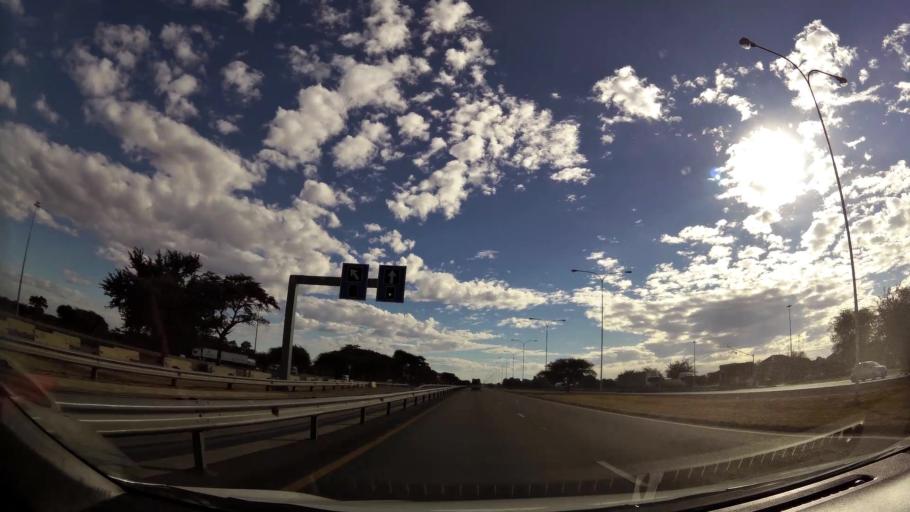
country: ZA
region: North-West
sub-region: Bojanala Platinum District Municipality
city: Makapanstad
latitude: -25.1353
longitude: 28.3096
